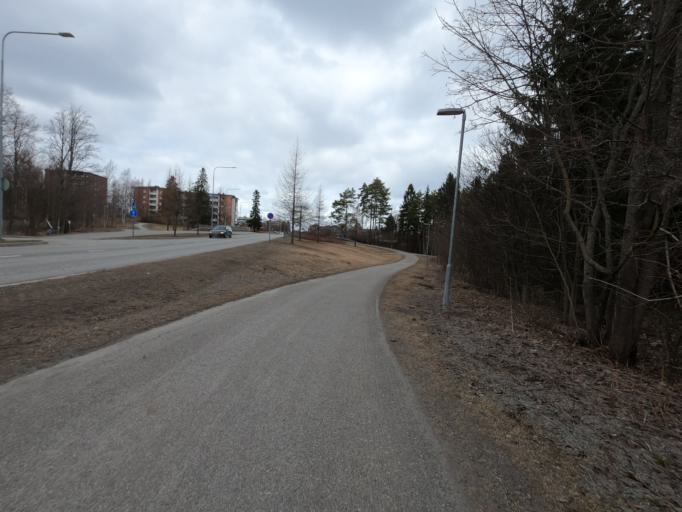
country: FI
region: North Karelia
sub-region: Joensuu
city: Joensuu
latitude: 62.5869
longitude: 29.7929
